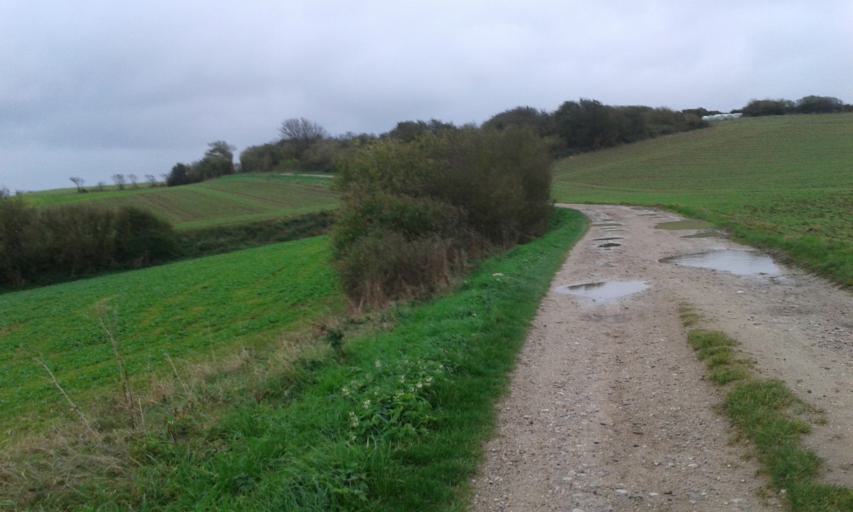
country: FR
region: Nord-Pas-de-Calais
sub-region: Departement du Pas-de-Calais
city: Wissant
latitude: 50.8854
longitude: 1.6937
